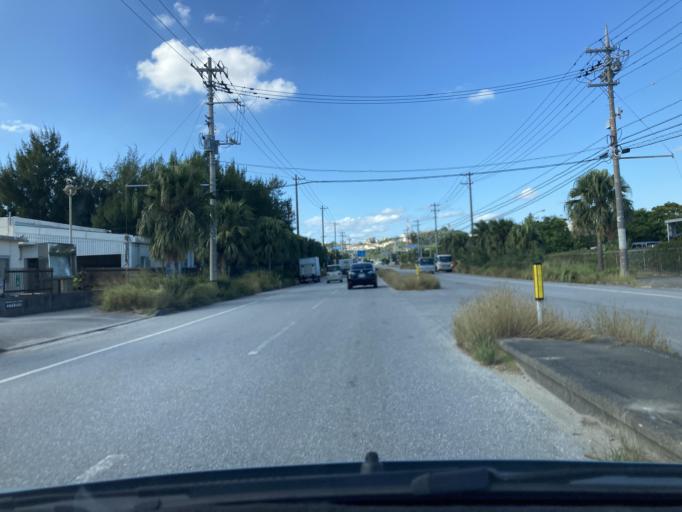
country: JP
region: Okinawa
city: Katsuren-haebaru
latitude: 26.3302
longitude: 127.8414
